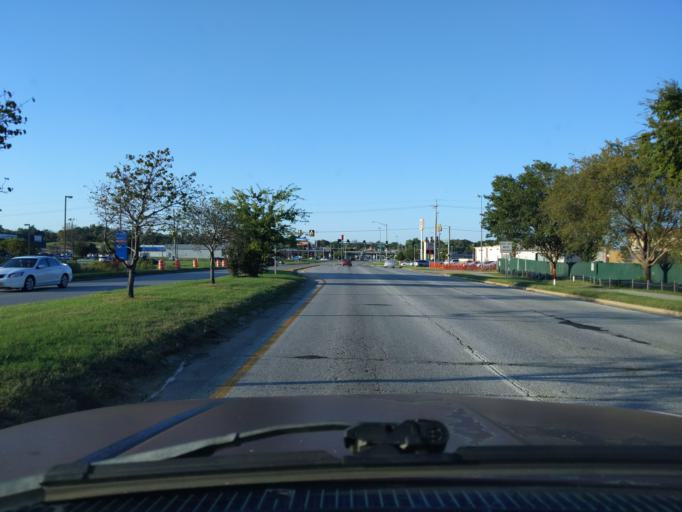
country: US
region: Oklahoma
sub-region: Tulsa County
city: Sand Springs
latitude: 36.1324
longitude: -96.1159
